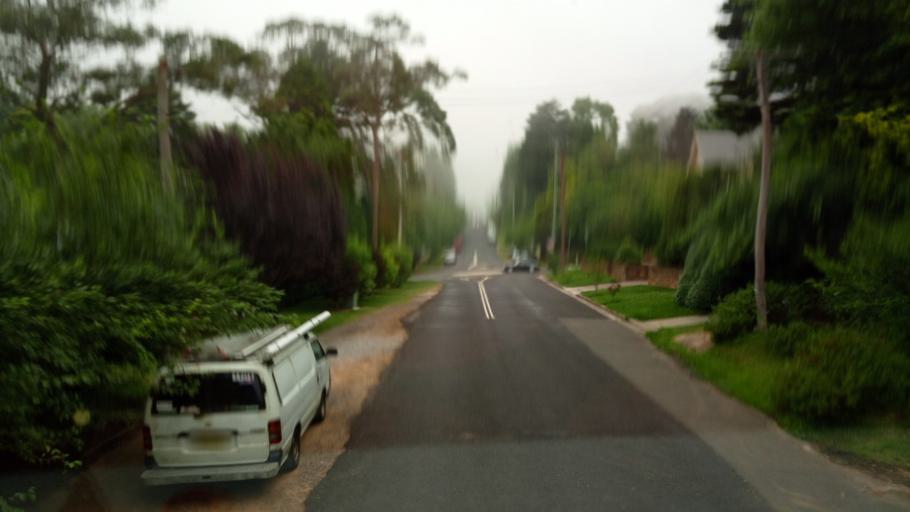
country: AU
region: New South Wales
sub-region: Blue Mountains Municipality
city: Leura
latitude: -33.7156
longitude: 150.3370
